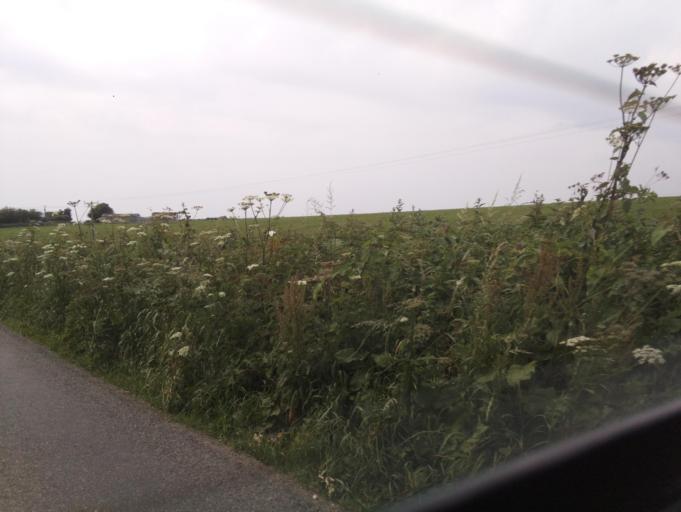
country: GB
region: England
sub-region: Devon
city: Colyton
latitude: 50.7227
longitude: -3.0180
